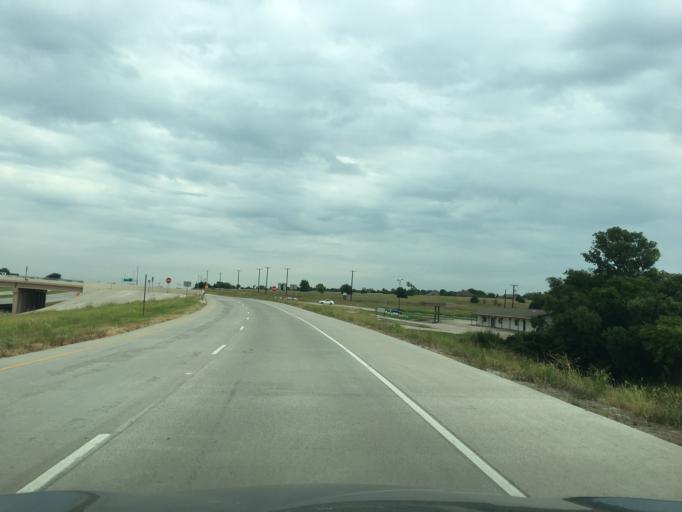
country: US
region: Texas
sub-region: Collin County
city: Melissa
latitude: 33.2834
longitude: -96.5917
